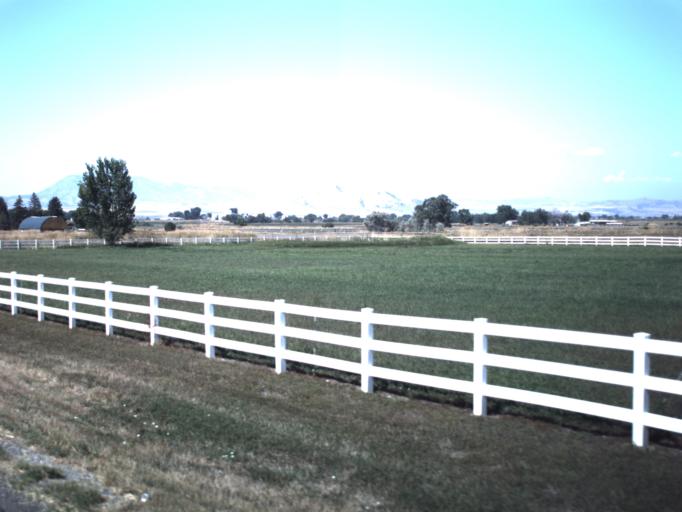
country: US
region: Utah
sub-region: Cache County
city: Smithfield
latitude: 41.8388
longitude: -111.8651
